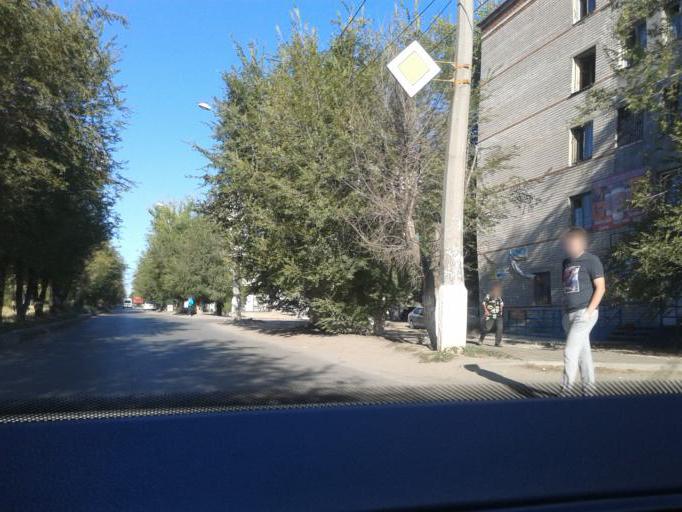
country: RU
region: Volgograd
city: Gorodishche
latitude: 48.7681
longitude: 44.4897
